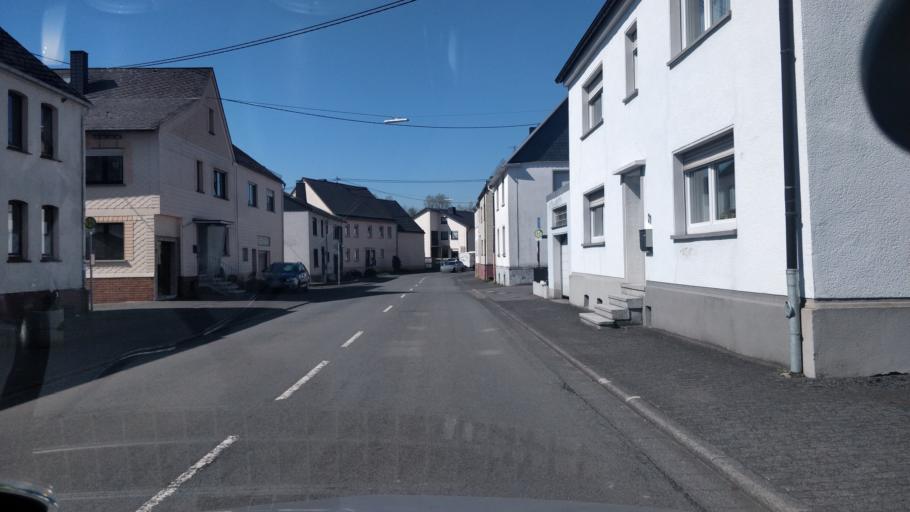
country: DE
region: Rheinland-Pfalz
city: Winnen
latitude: 50.5720
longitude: 8.0100
